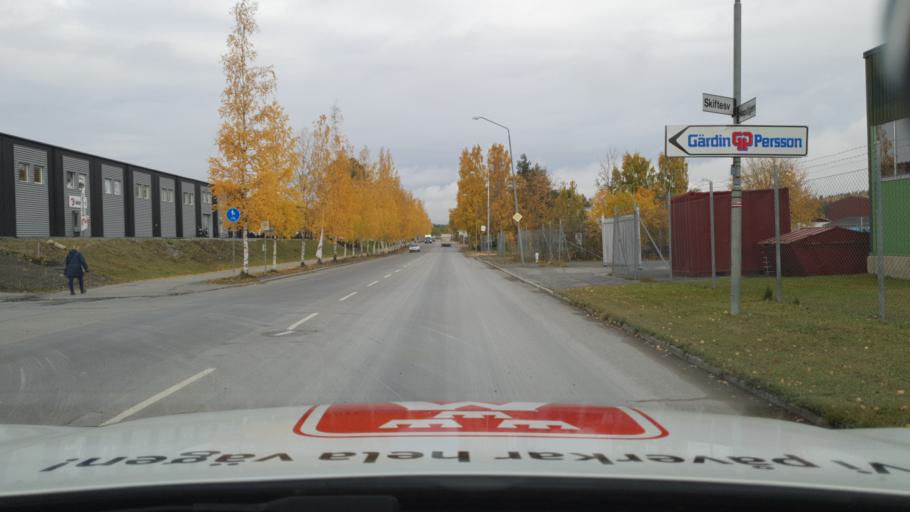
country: SE
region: Jaemtland
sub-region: OEstersunds Kommun
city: Ostersund
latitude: 63.1663
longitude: 14.6894
